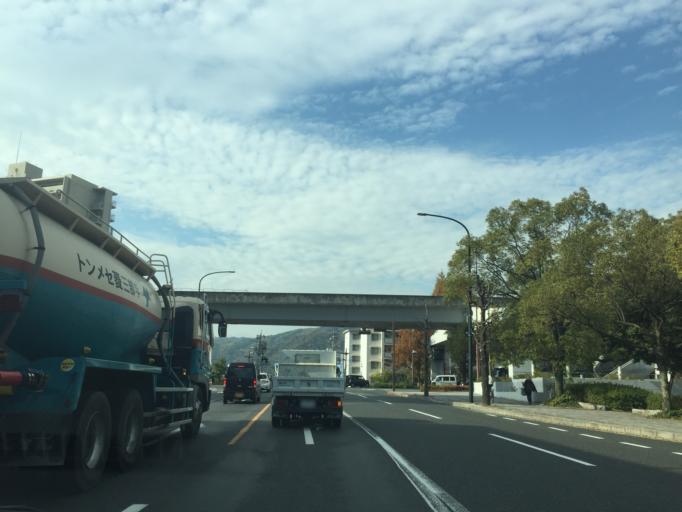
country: JP
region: Hiroshima
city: Hiroshima-shi
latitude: 34.4163
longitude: 132.4653
